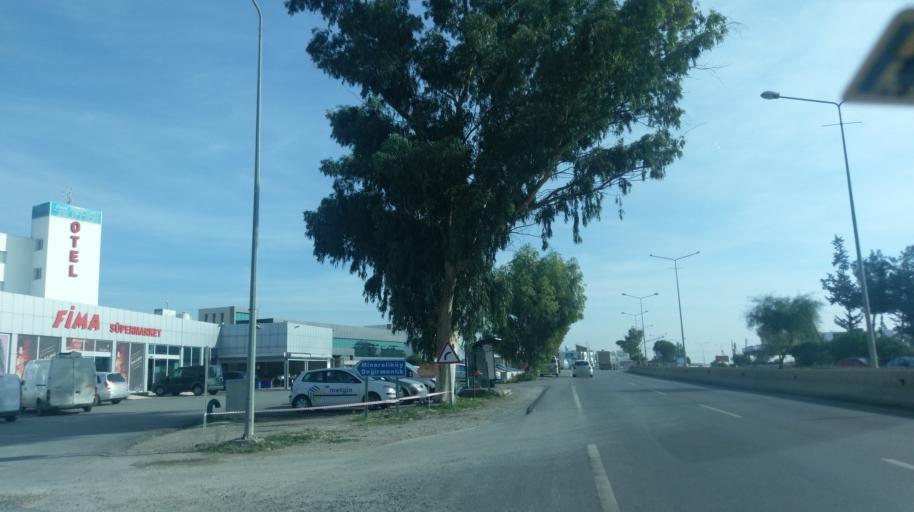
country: CY
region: Lefkosia
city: Nicosia
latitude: 35.2219
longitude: 33.4812
